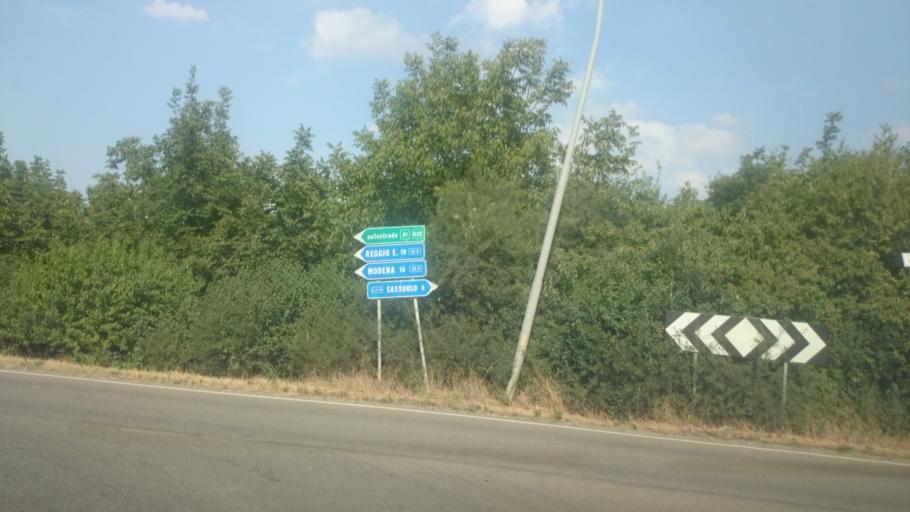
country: IT
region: Emilia-Romagna
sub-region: Provincia di Reggio Emilia
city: Salvaterra
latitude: 44.6052
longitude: 10.7767
